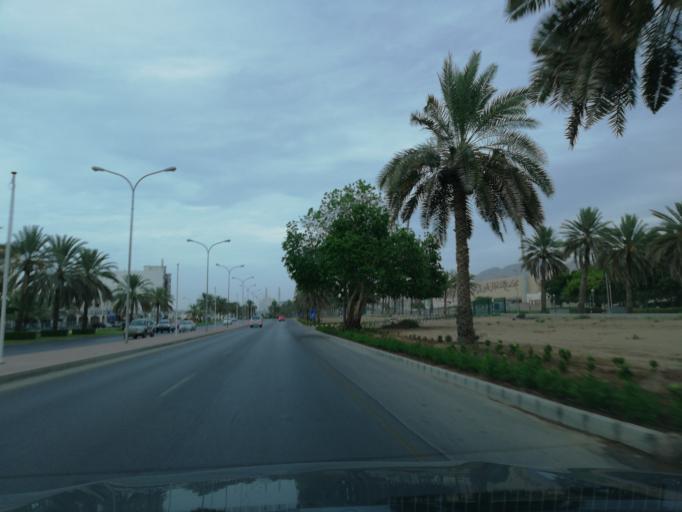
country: OM
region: Muhafazat Masqat
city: Bawshar
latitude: 23.5740
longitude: 58.3960
